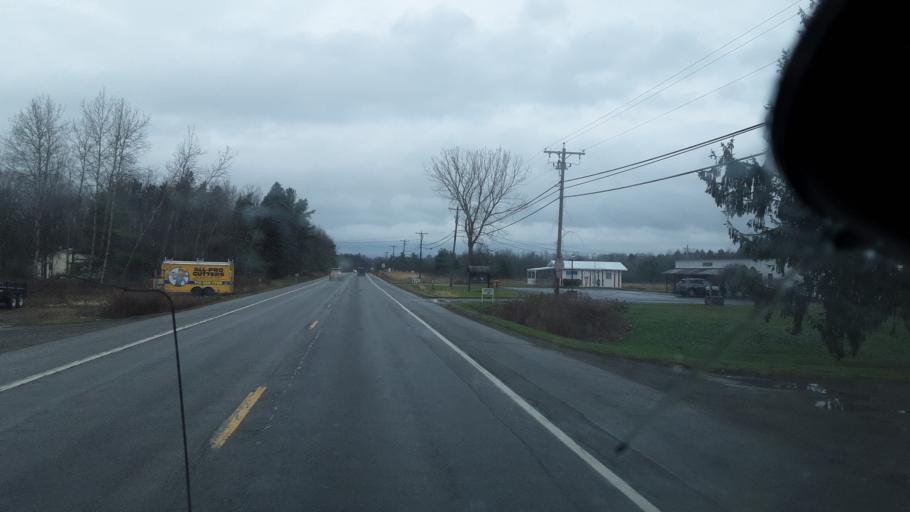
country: US
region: New York
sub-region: Cattaraugus County
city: Delevan
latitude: 42.5012
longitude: -78.4799
